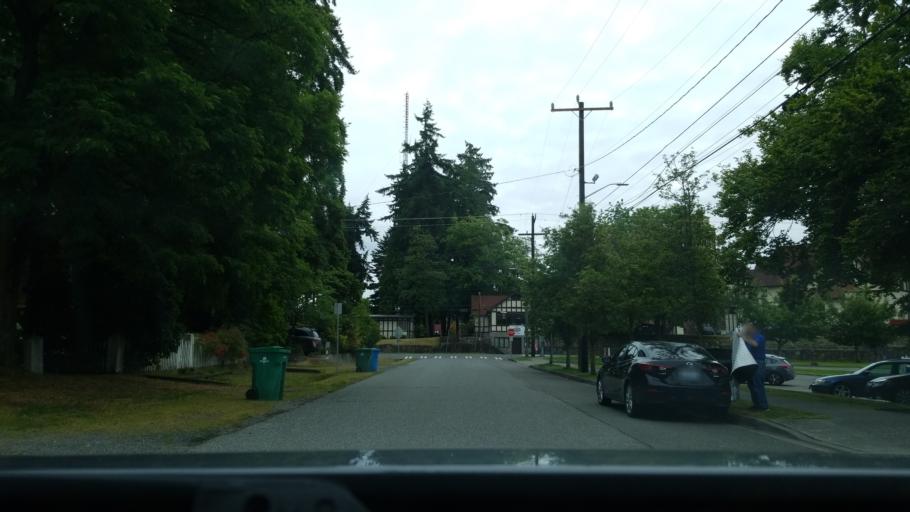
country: US
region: Washington
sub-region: Snohomish County
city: Esperance
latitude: 47.7712
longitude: -122.3536
